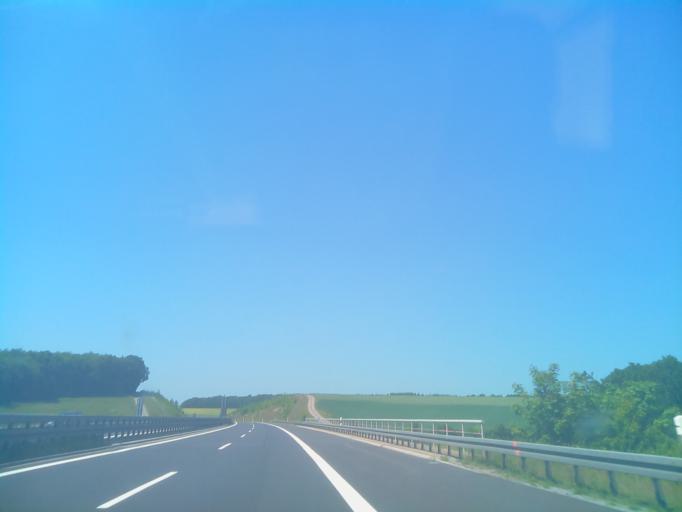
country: DE
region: Bavaria
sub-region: Regierungsbezirk Unterfranken
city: Poppenhausen
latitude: 50.1084
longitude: 10.1629
